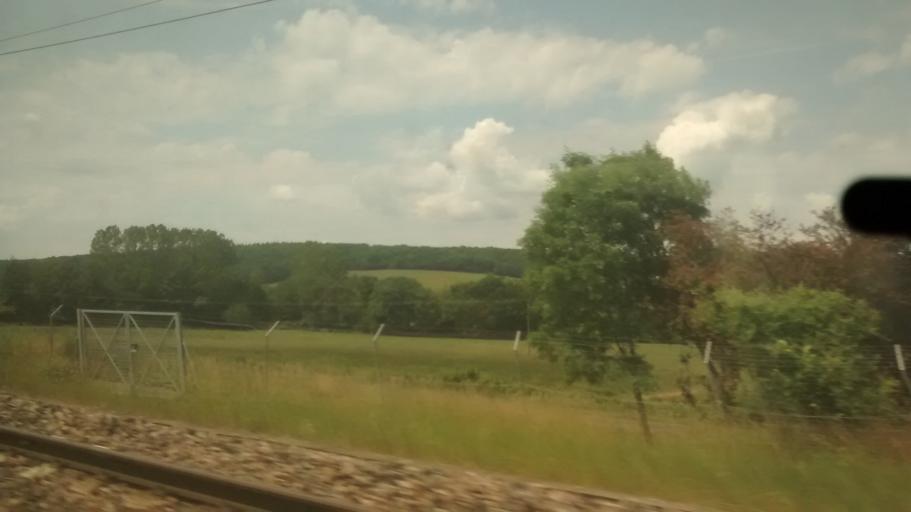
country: FR
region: Bourgogne
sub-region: Departement de Saone-et-Loire
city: Cluny
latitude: 46.4155
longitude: 4.6617
